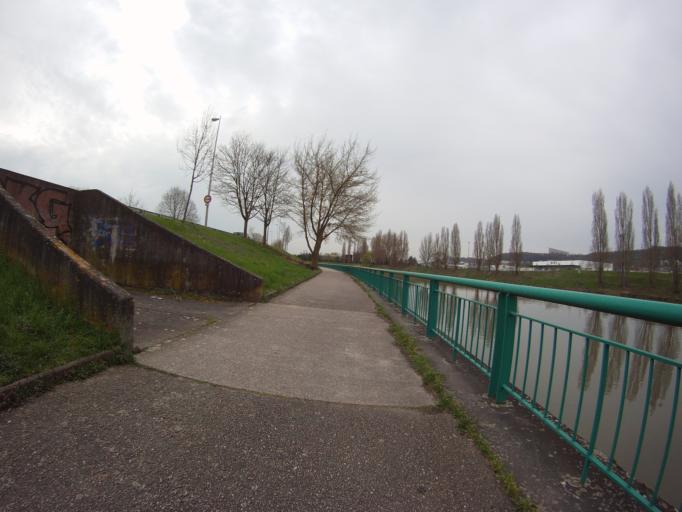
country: FR
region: Lorraine
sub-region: Departement de Meurthe-et-Moselle
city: Malzeville
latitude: 48.7164
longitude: 6.1743
